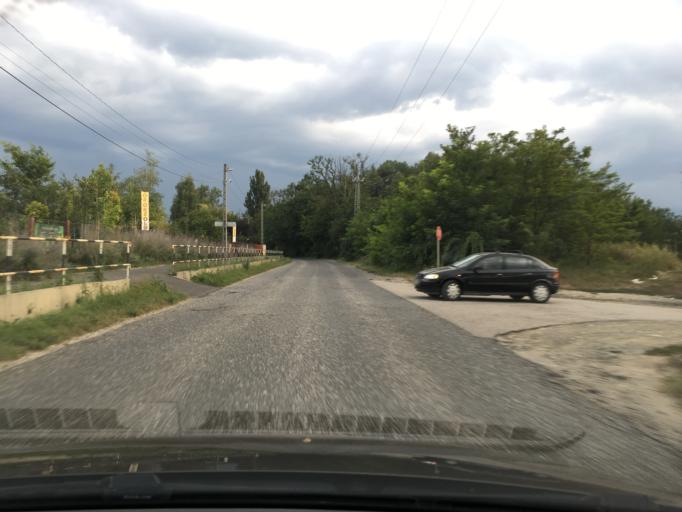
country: HU
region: Pest
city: Szada
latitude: 47.6267
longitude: 19.3009
